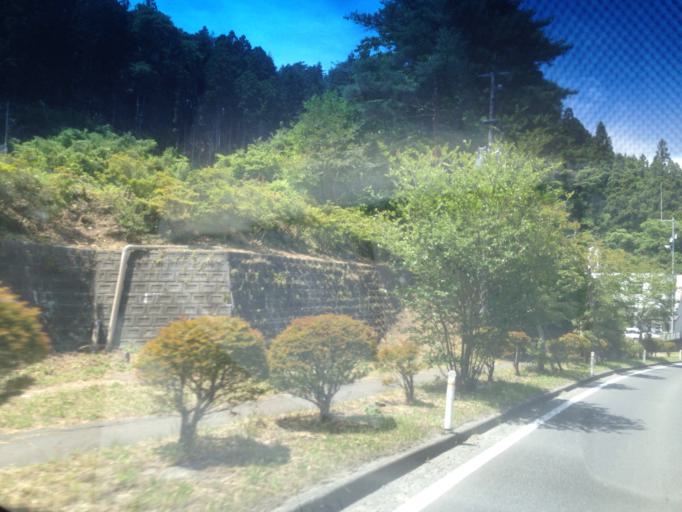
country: JP
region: Iwate
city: Kamaishi
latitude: 39.3171
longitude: 141.8836
